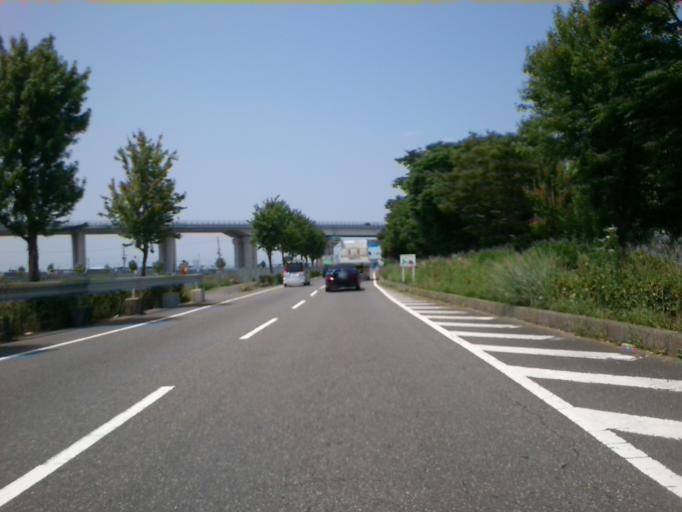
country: JP
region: Kyoto
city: Uji
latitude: 34.9004
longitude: 135.7638
